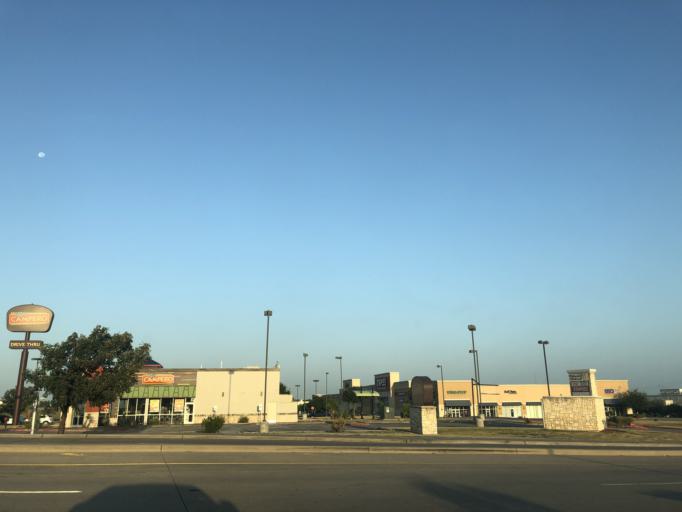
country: US
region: Texas
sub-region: Dallas County
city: Cockrell Hill
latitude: 32.7681
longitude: -96.8958
